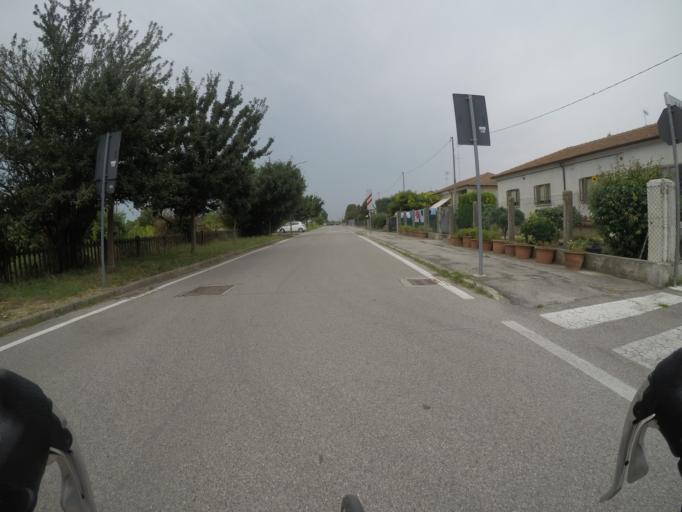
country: IT
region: Veneto
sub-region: Provincia di Rovigo
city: Costa di Rovigo
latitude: 45.0456
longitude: 11.6952
